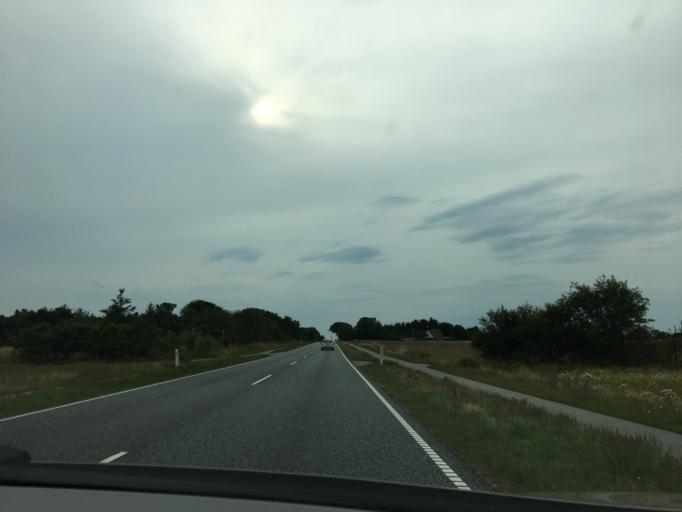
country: DK
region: Central Jutland
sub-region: Ringkobing-Skjern Kommune
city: Ringkobing
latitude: 56.0867
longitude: 8.2934
